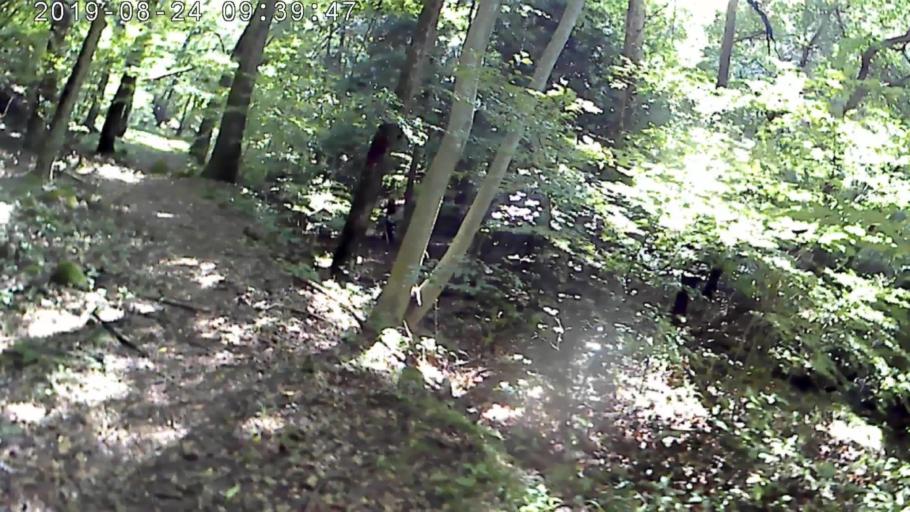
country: JP
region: Nagano
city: Kamimaruko
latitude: 36.2522
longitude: 138.2828
